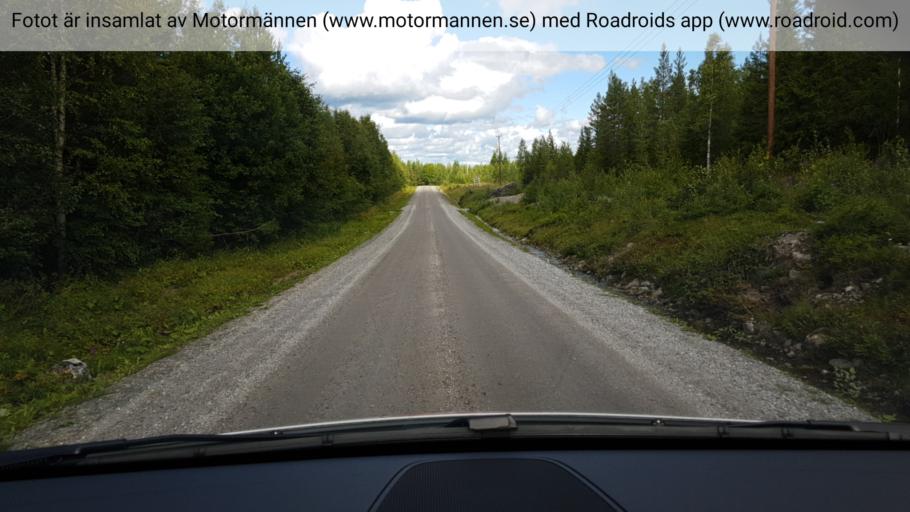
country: SE
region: Jaemtland
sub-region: Braecke Kommun
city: Braecke
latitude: 63.0900
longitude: 15.7351
